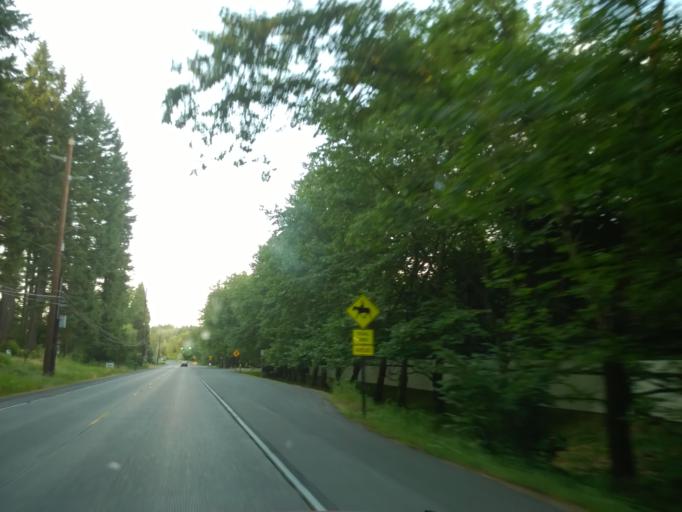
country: US
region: Washington
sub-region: King County
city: Cottage Lake
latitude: 47.7355
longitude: -122.0808
